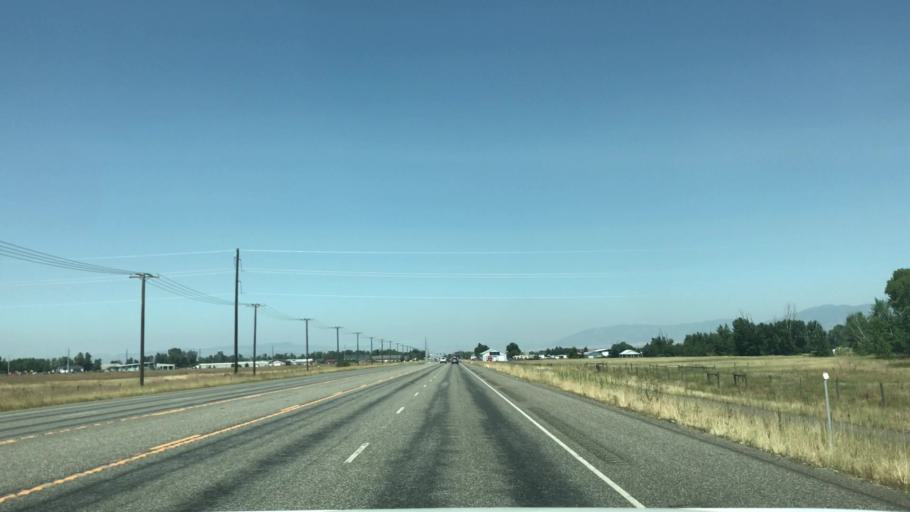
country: US
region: Montana
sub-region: Gallatin County
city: Four Corners
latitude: 45.6917
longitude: -111.1856
